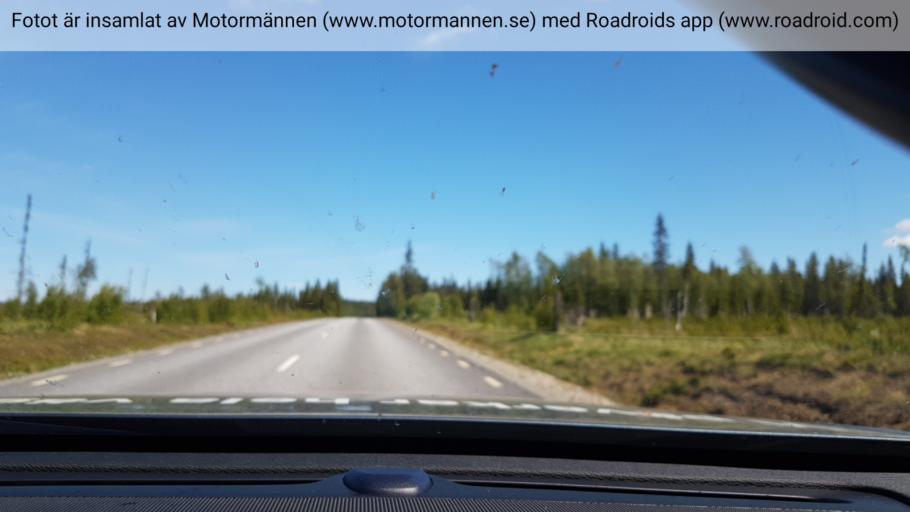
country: SE
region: Vaesterbotten
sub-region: Asele Kommun
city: Insjon
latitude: 64.7039
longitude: 17.2301
